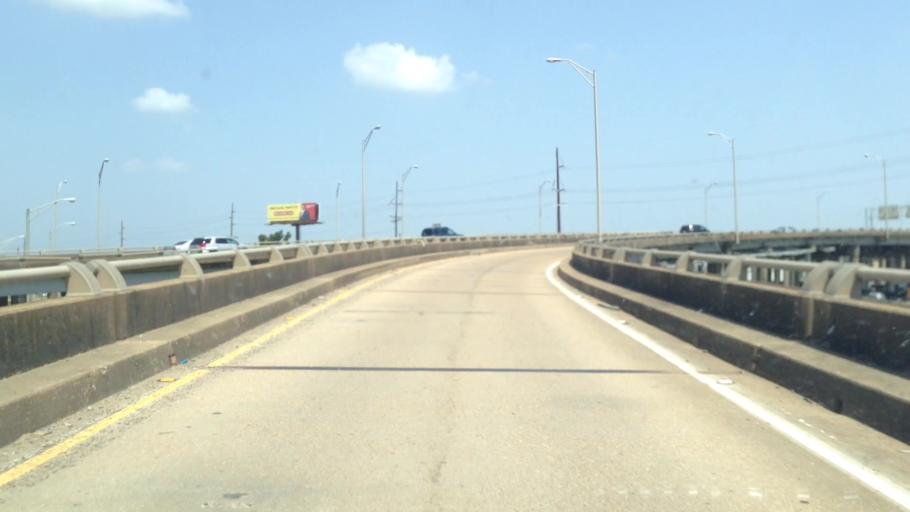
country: US
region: Louisiana
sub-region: Ouachita Parish
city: Monroe
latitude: 32.5009
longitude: -92.0820
